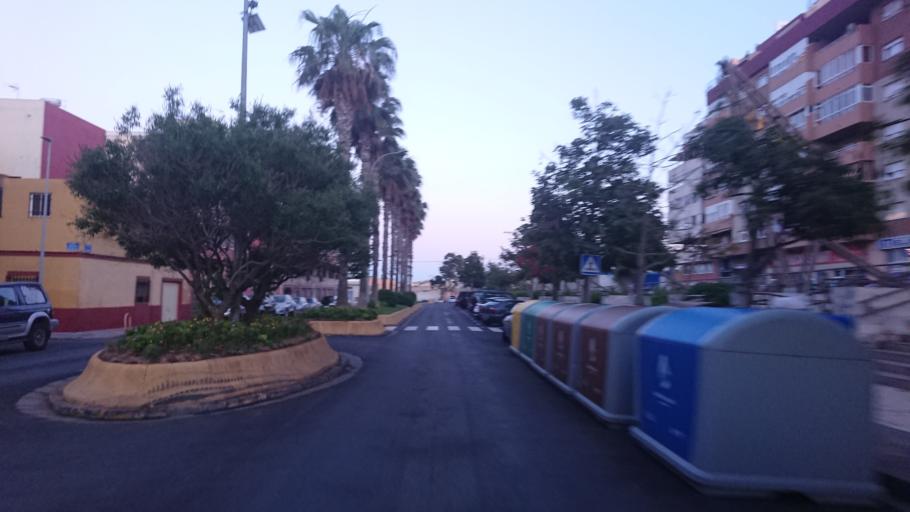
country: ES
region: Melilla
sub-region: Melilla
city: Melilla
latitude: 35.2738
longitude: -2.9471
